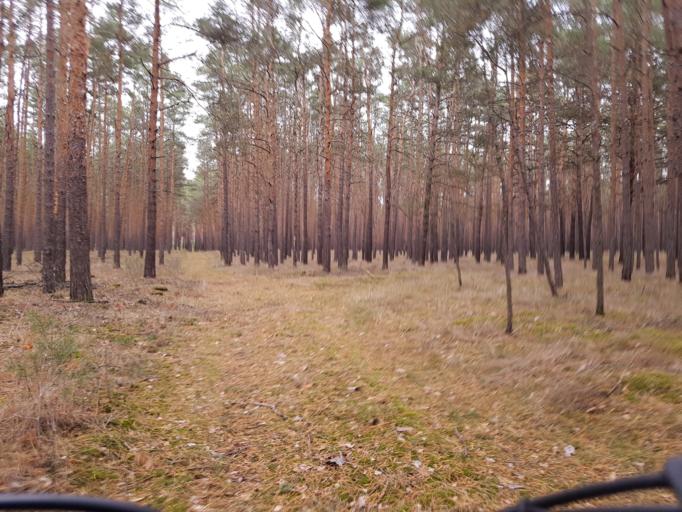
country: DE
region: Brandenburg
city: Schilda
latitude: 51.6140
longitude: 13.3777
